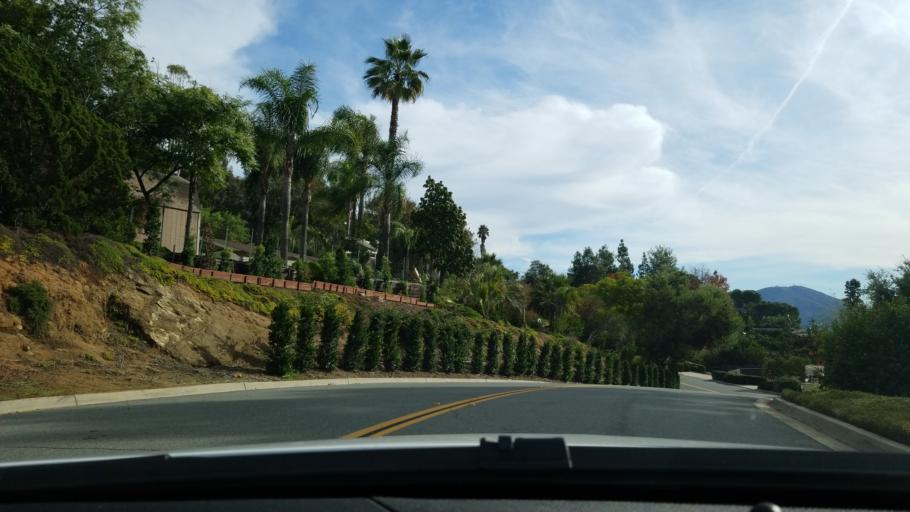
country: US
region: California
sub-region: San Diego County
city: Casa de Oro-Mount Helix
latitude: 32.7688
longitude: -116.9531
